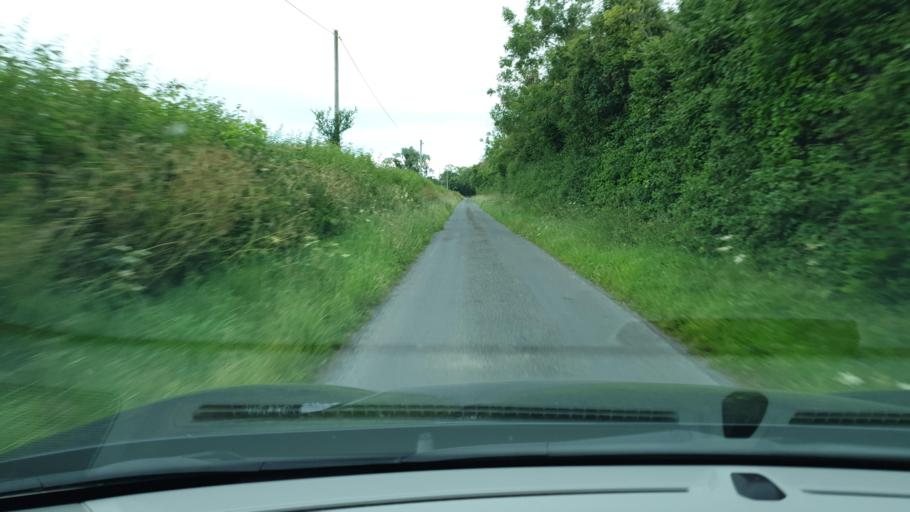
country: IE
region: Leinster
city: Ballymun
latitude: 53.4306
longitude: -6.2866
